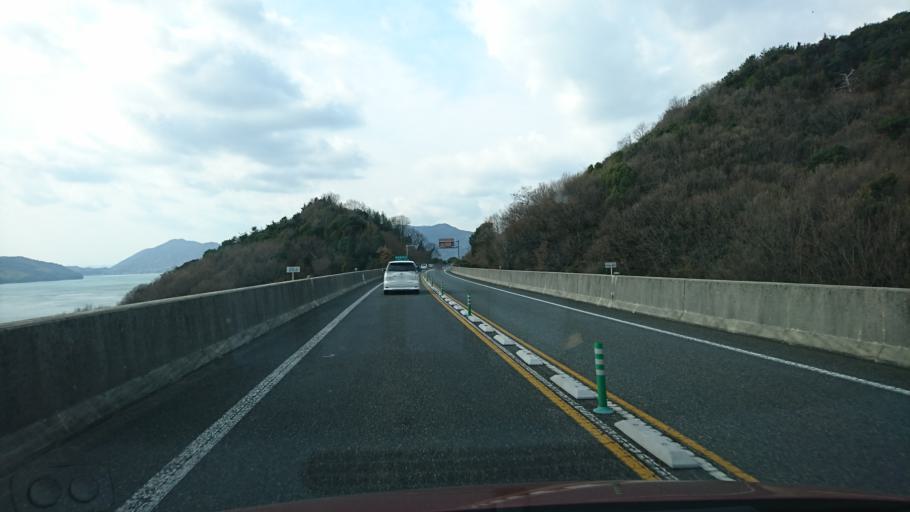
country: JP
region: Hiroshima
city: Innoshima
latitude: 34.2608
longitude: 133.0893
